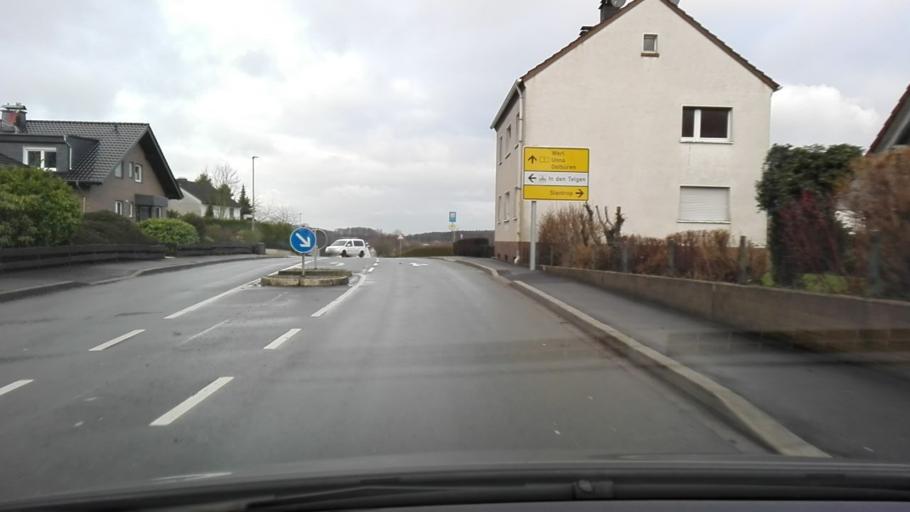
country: DE
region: North Rhine-Westphalia
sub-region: Regierungsbezirk Arnsberg
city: Frondenberg
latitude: 51.4897
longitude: 7.7814
